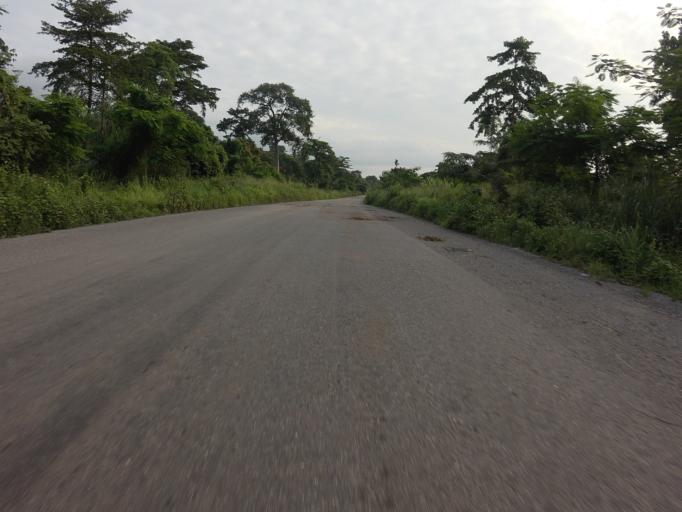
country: GH
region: Volta
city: Kpandu
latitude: 6.8723
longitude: 0.4200
